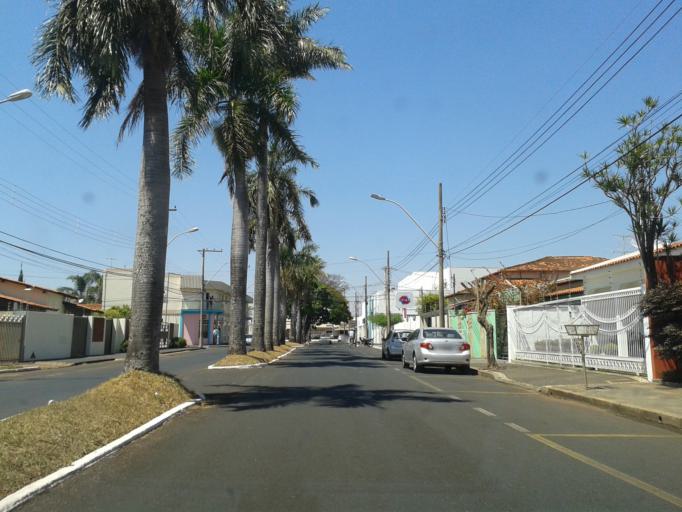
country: BR
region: Minas Gerais
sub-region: Araguari
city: Araguari
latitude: -18.6586
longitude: -48.1871
